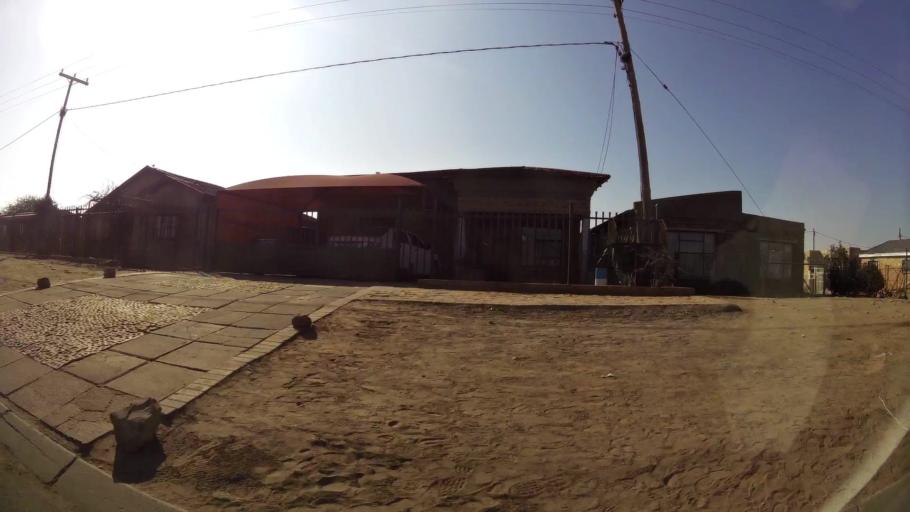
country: ZA
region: Orange Free State
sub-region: Mangaung Metropolitan Municipality
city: Bloemfontein
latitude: -29.1970
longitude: 26.2478
